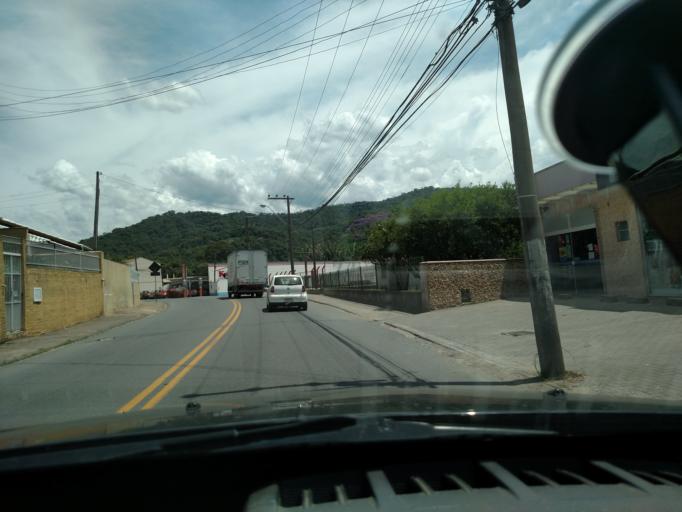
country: BR
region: Santa Catarina
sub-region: Blumenau
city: Blumenau
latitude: -26.9708
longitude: -49.0759
